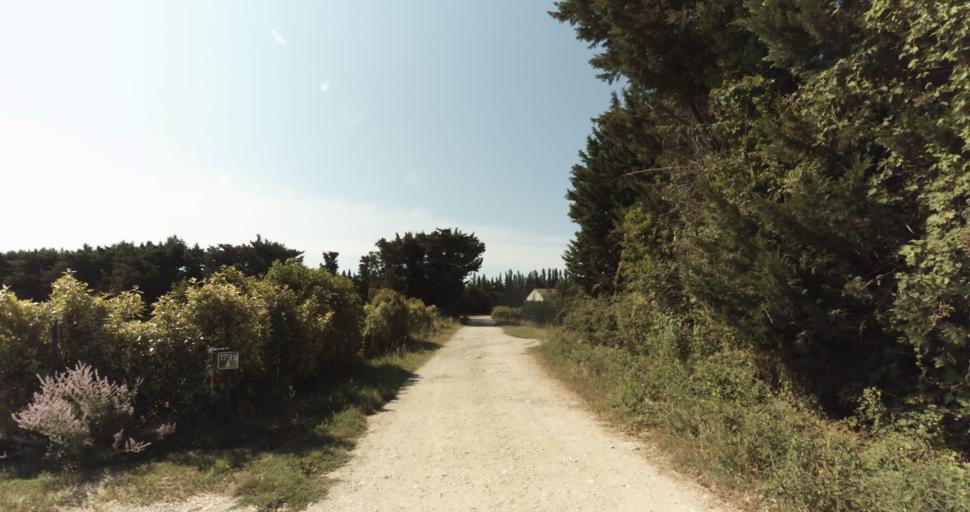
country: FR
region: Provence-Alpes-Cote d'Azur
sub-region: Departement du Vaucluse
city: Monteux
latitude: 44.0154
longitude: 4.9891
